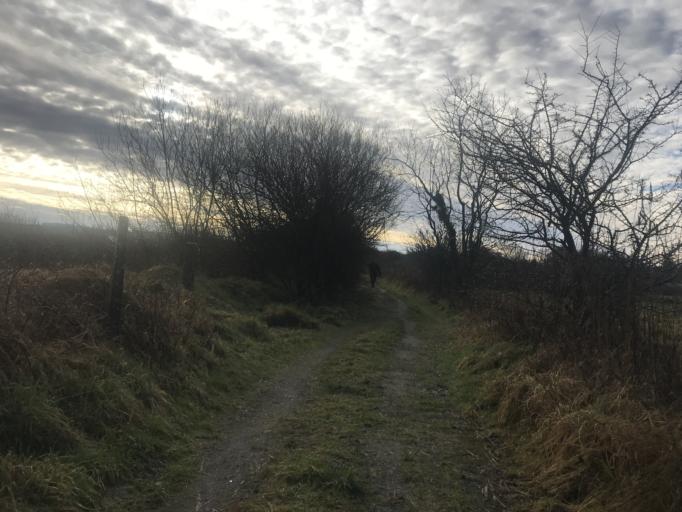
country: IE
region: Connaught
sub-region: County Galway
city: Claregalway
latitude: 53.3177
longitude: -9.0046
